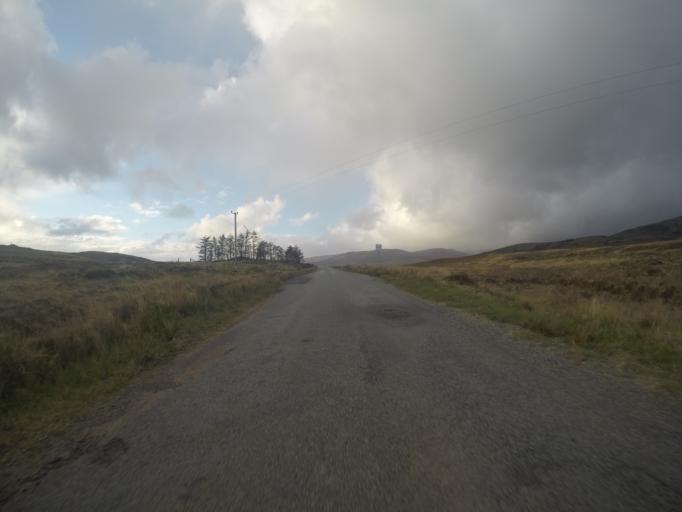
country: GB
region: Scotland
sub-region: Highland
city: Isle of Skye
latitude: 57.4578
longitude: -6.2970
